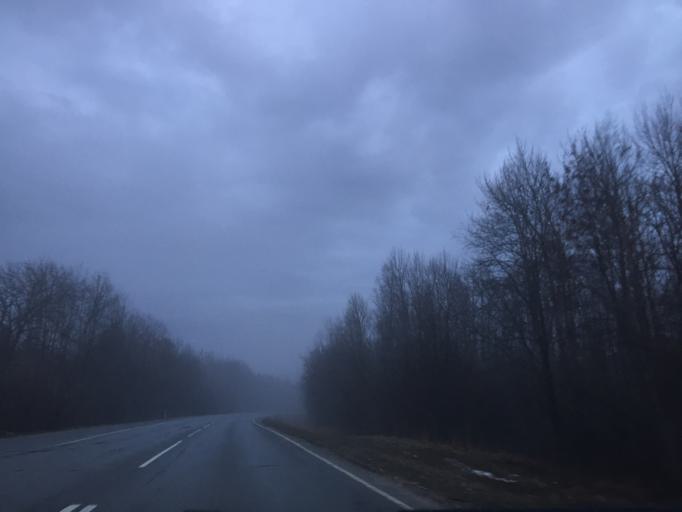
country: EE
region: Laeaene
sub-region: Lihula vald
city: Lihula
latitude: 58.6836
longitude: 23.8105
